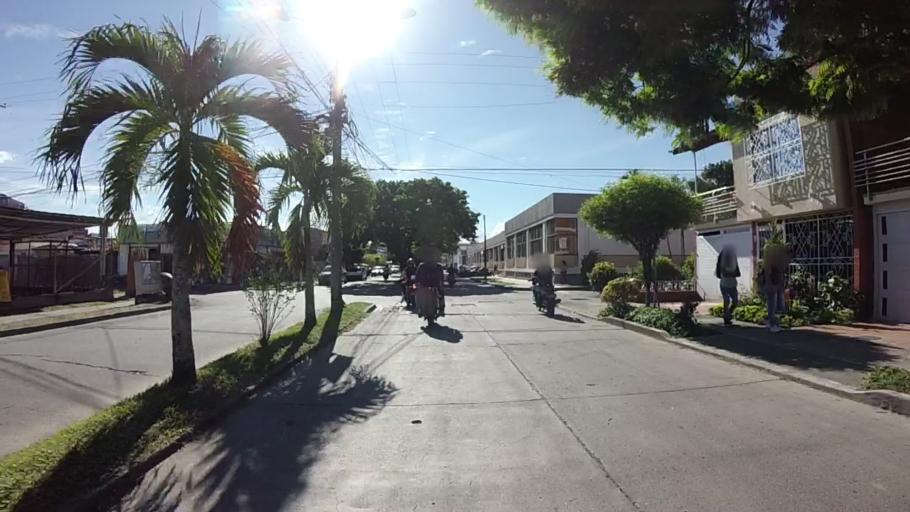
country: CO
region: Valle del Cauca
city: Cartago
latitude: 4.7575
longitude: -75.9200
